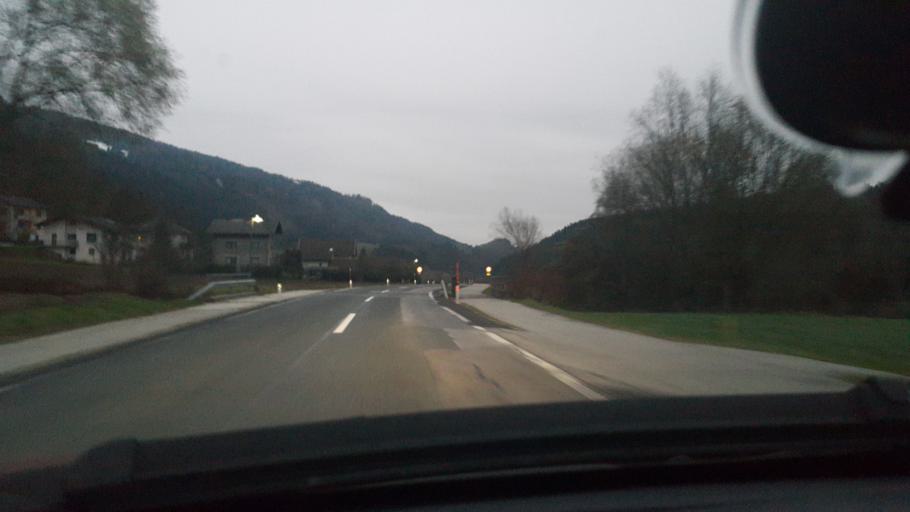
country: AT
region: Carinthia
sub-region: Politischer Bezirk Wolfsberg
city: Lavamund
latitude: 46.6345
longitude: 14.9585
